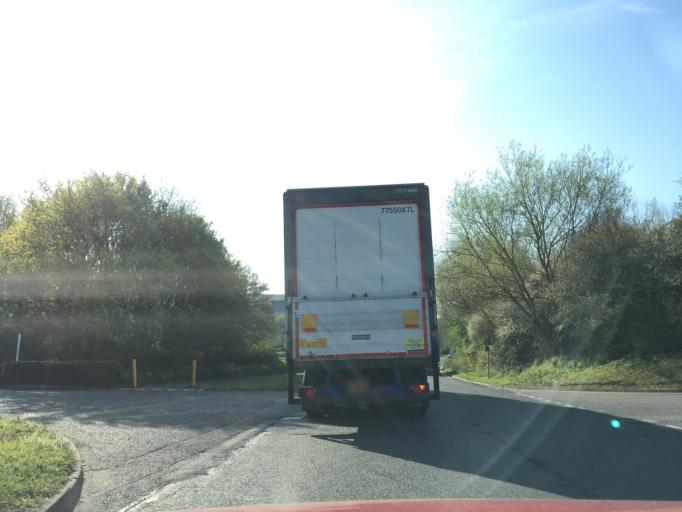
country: GB
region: England
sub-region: Milton Keynes
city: Newport Pagnell
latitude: 52.0677
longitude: -0.7293
